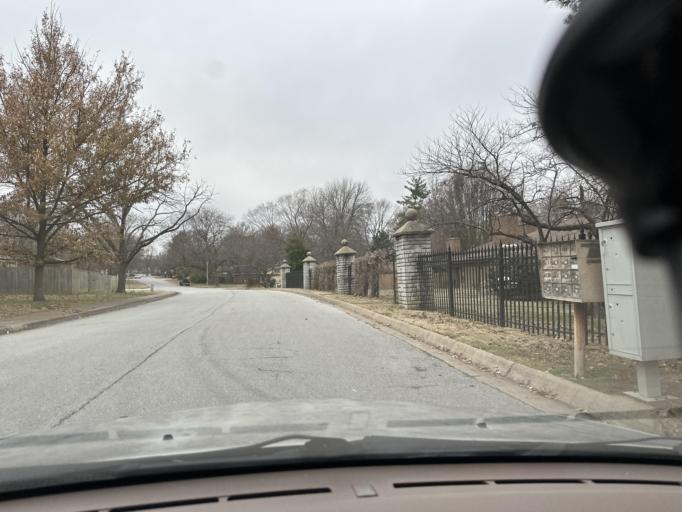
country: US
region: Arkansas
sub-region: Washington County
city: Fayetteville
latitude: 36.0858
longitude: -94.1133
